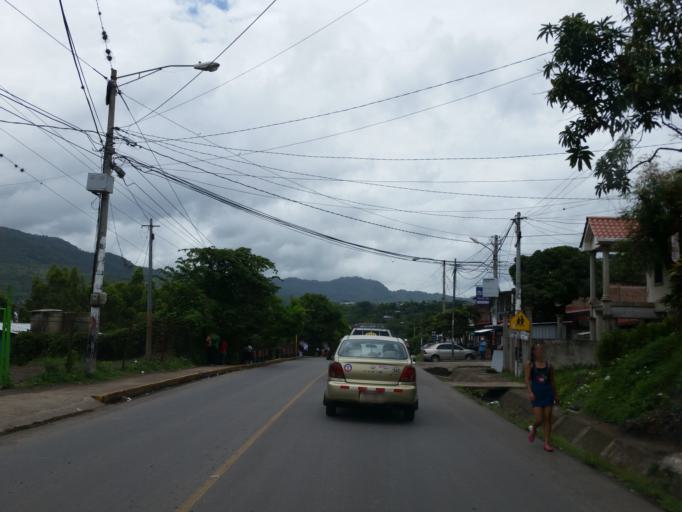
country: NI
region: Matagalpa
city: Matagalpa
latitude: 12.9347
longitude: -85.9202
